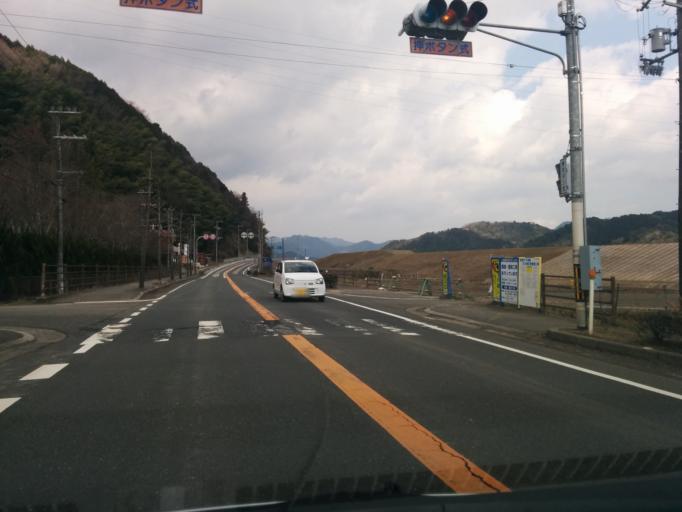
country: JP
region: Kyoto
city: Maizuru
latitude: 35.4383
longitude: 135.2555
